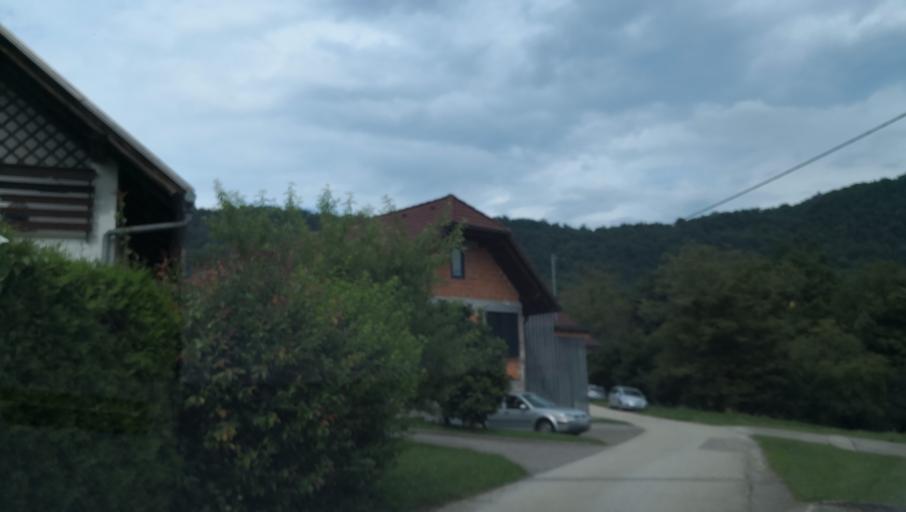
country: SI
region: Zuzemberk
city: Zuzemberk
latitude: 45.7944
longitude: 14.9791
